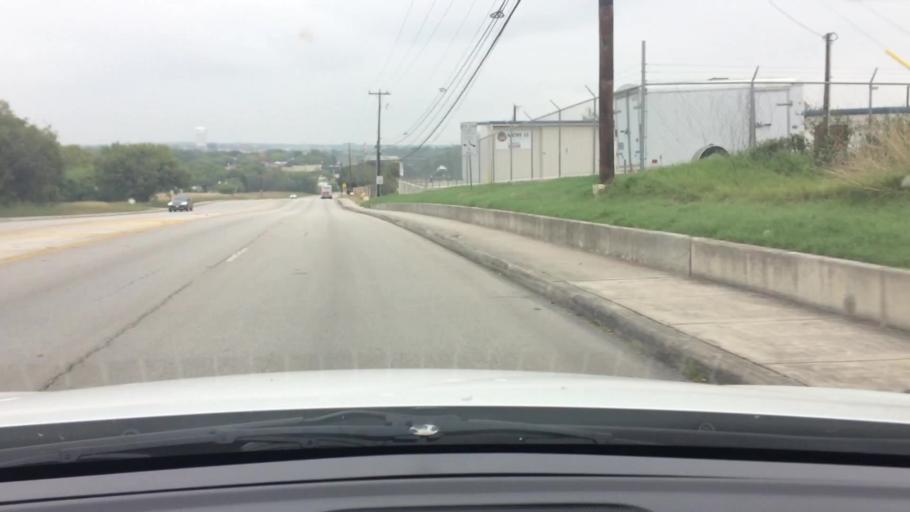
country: US
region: Texas
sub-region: Bexar County
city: Converse
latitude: 29.5231
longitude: -98.3440
